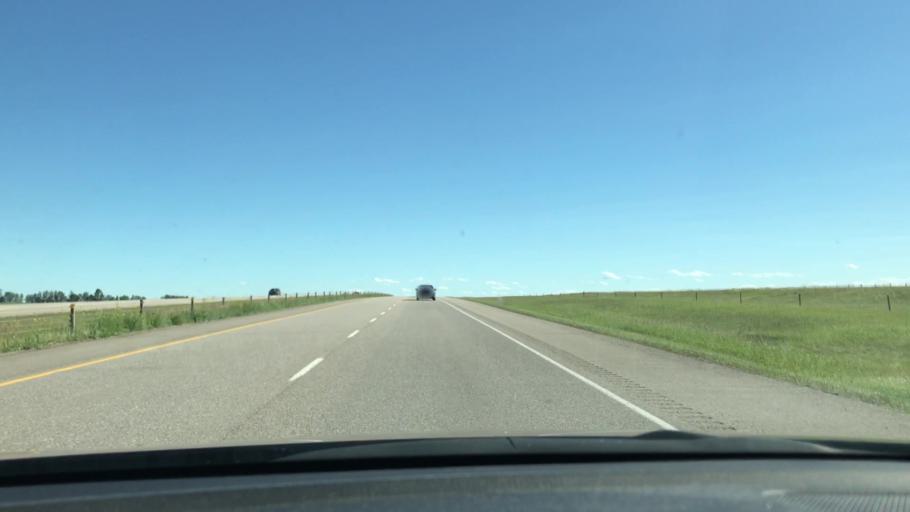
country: CA
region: Alberta
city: Carstairs
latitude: 51.6316
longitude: -114.0256
